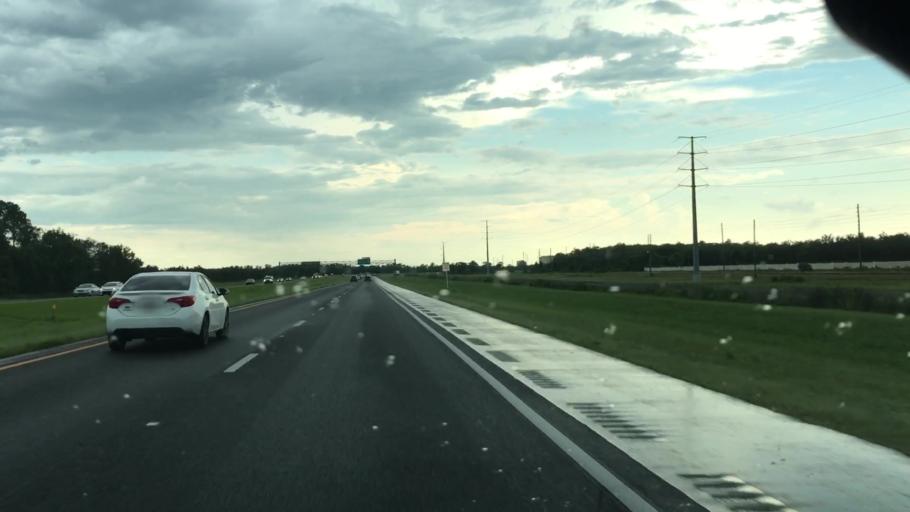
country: US
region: Florida
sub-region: Orange County
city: Meadow Woods
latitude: 28.3920
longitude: -81.2544
